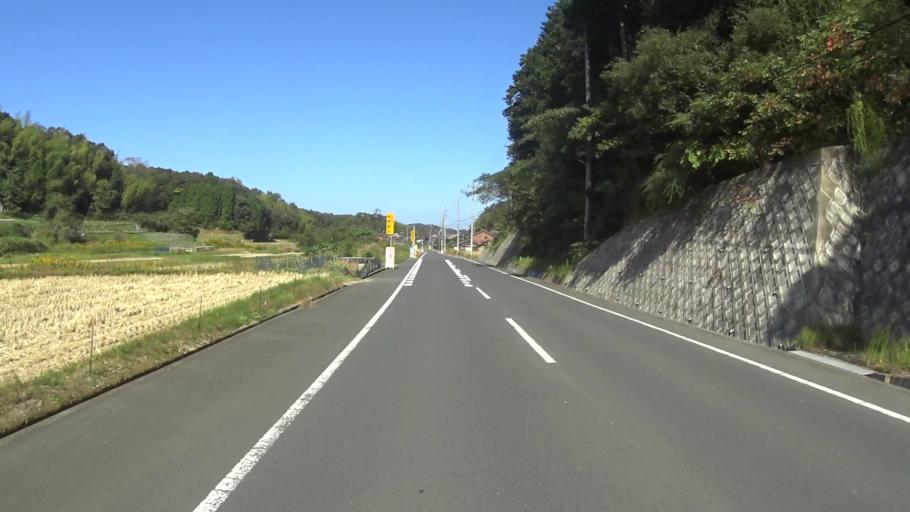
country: JP
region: Kyoto
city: Miyazu
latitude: 35.6738
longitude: 135.0557
